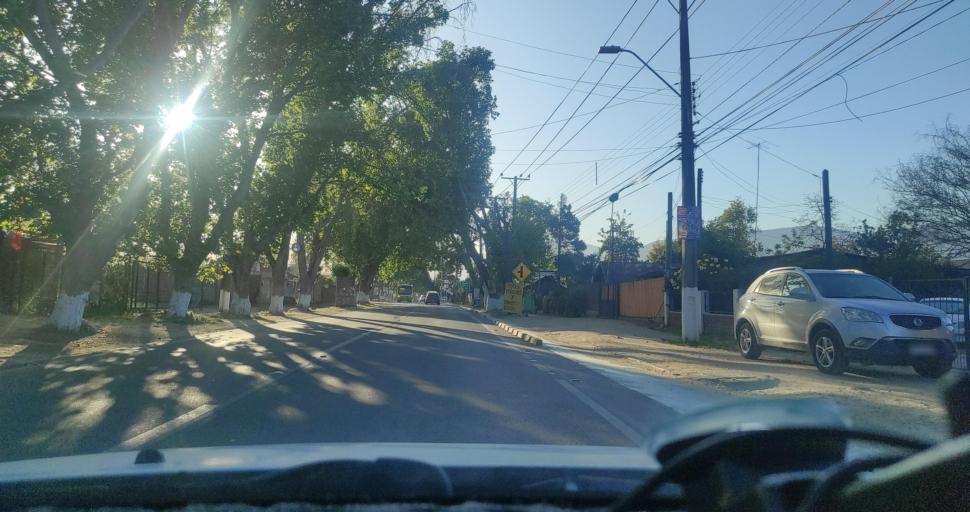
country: CL
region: Valparaiso
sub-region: Provincia de Marga Marga
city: Limache
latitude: -32.9985
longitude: -71.2168
